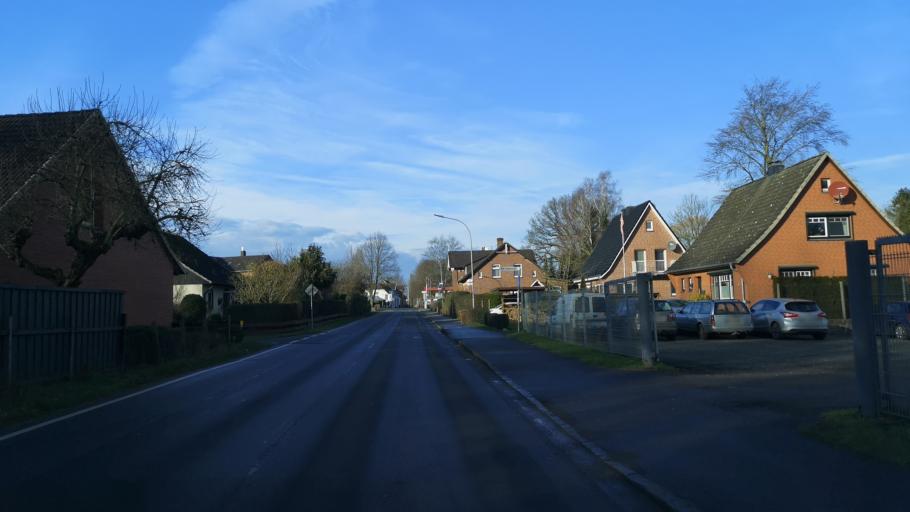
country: DE
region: Schleswig-Holstein
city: Lagerdorf
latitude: 53.8837
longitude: 9.5805
